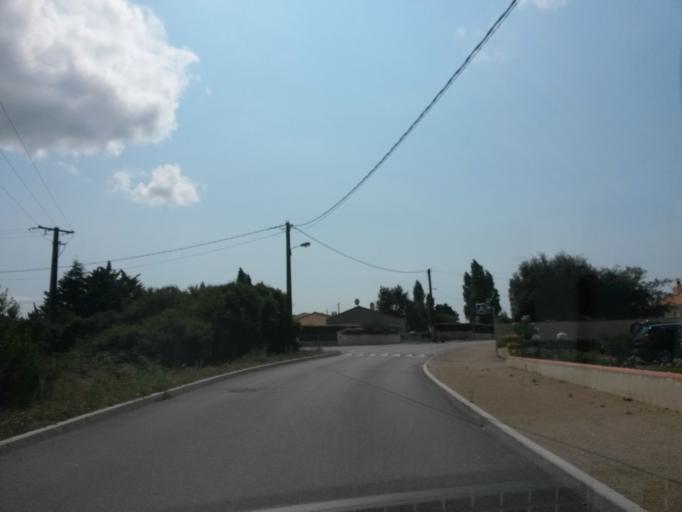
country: FR
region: Pays de la Loire
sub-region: Departement de la Vendee
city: Saint-Hilaire-de-Talmont
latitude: 46.4492
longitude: -1.6245
